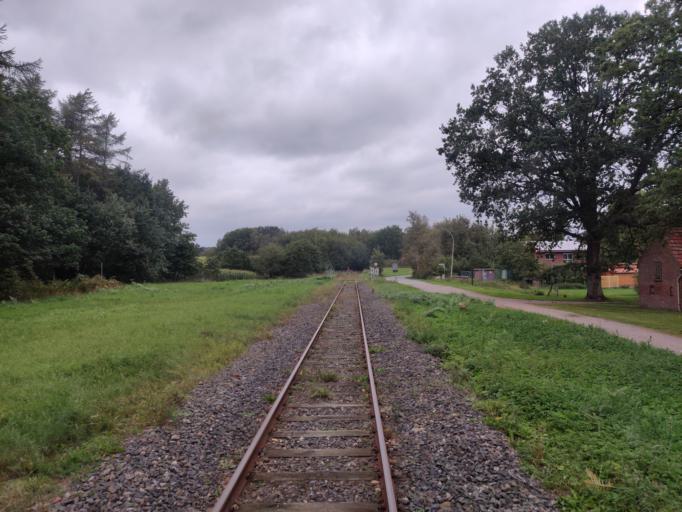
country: DE
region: Lower Saxony
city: Gnarrenburg
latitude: 53.4044
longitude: 9.0109
